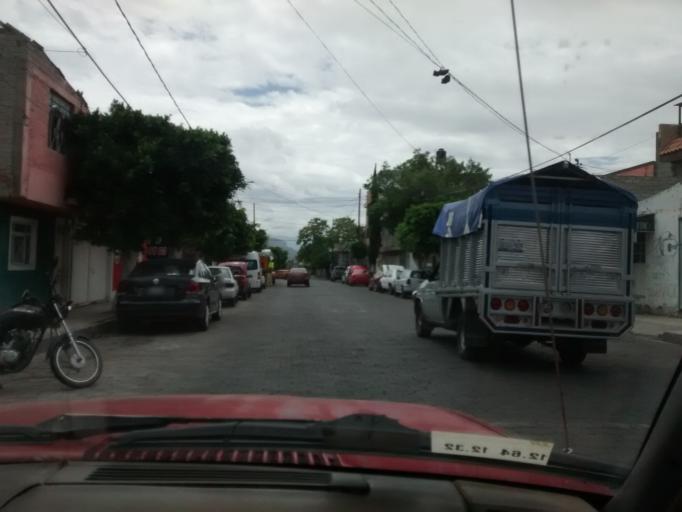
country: MX
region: Puebla
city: Tehuacan
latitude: 18.4674
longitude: -97.4014
